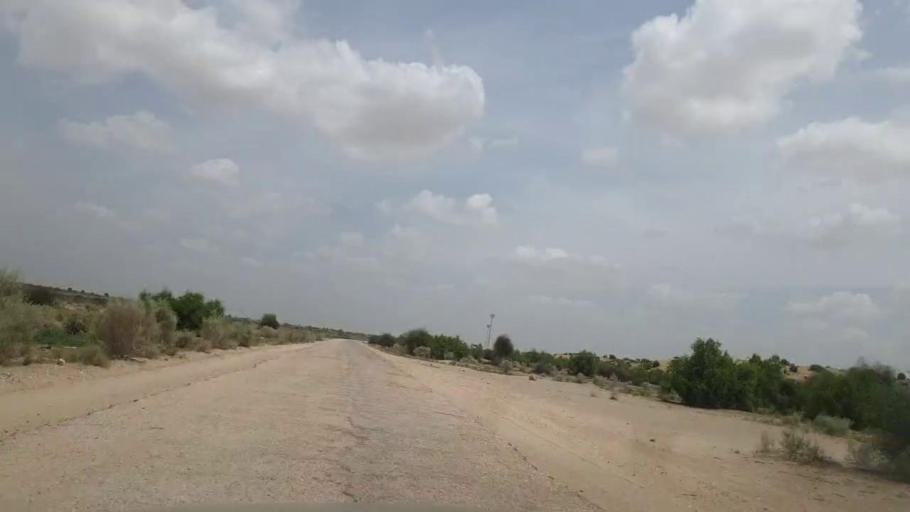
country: PK
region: Sindh
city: Kot Diji
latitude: 27.2026
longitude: 69.1469
